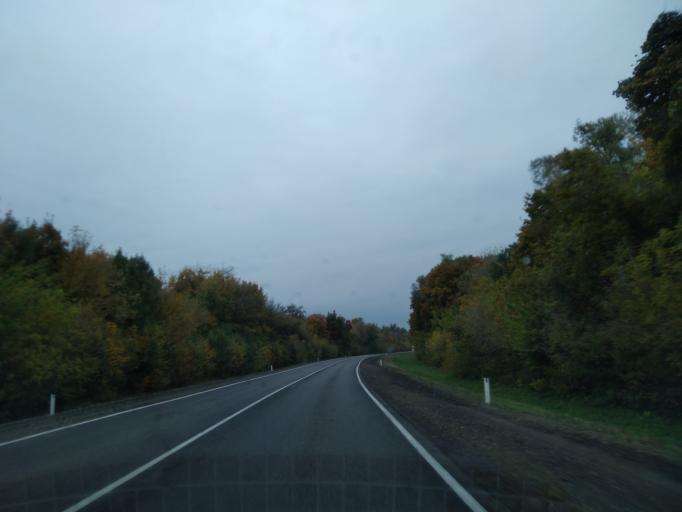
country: RU
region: Lipetsk
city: Zadonsk
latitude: 52.4905
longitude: 38.7576
